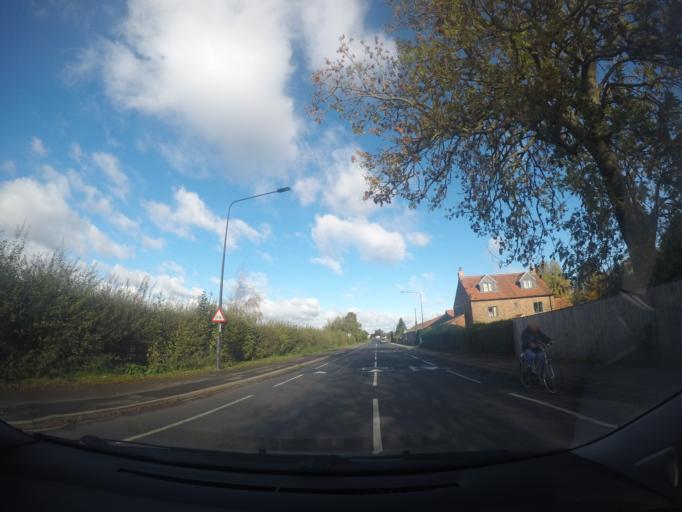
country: GB
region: England
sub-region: City of York
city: Haxby
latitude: 53.9987
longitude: -1.0724
